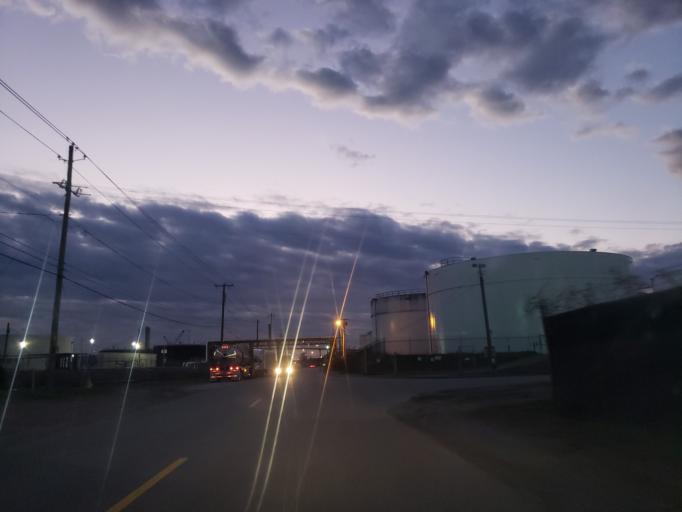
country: US
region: Georgia
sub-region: Chatham County
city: Savannah
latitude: 32.0950
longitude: -81.1136
